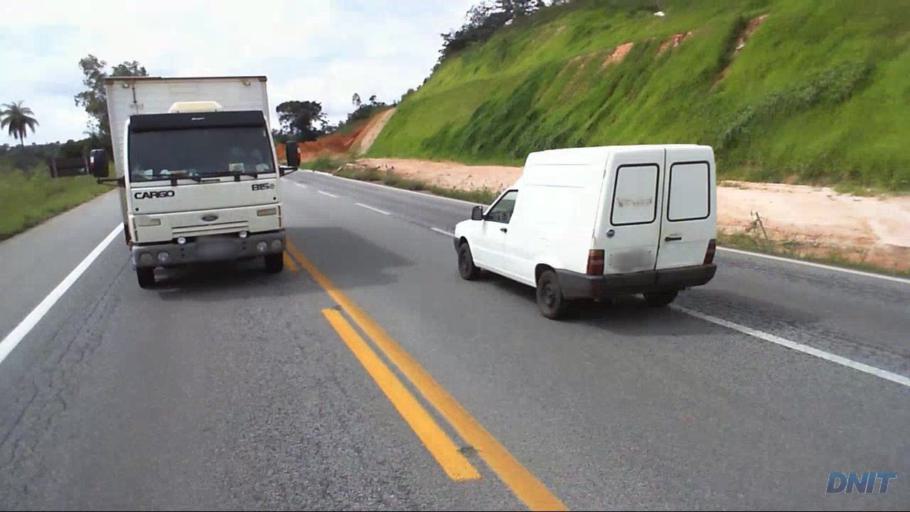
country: BR
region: Minas Gerais
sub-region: Caete
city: Caete
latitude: -19.7430
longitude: -43.6144
